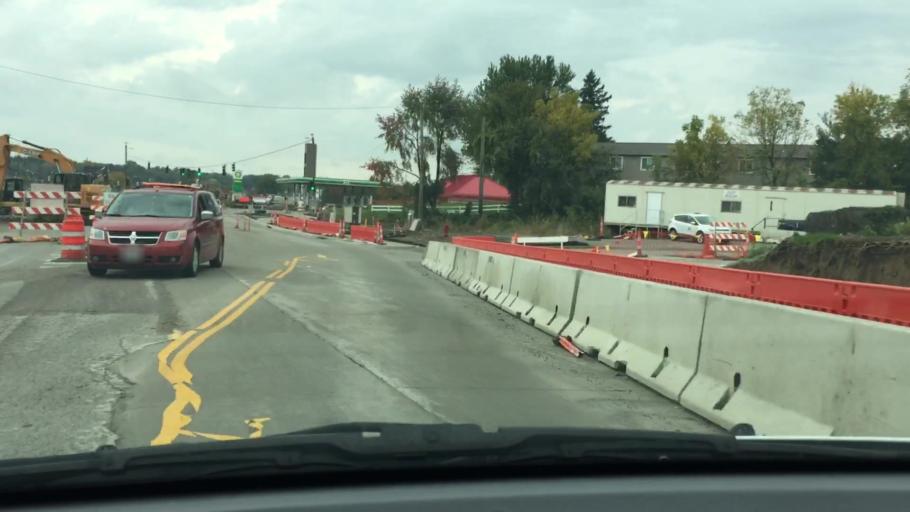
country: US
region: Iowa
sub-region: Johnson County
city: Coralville
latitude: 41.6779
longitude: -91.5660
